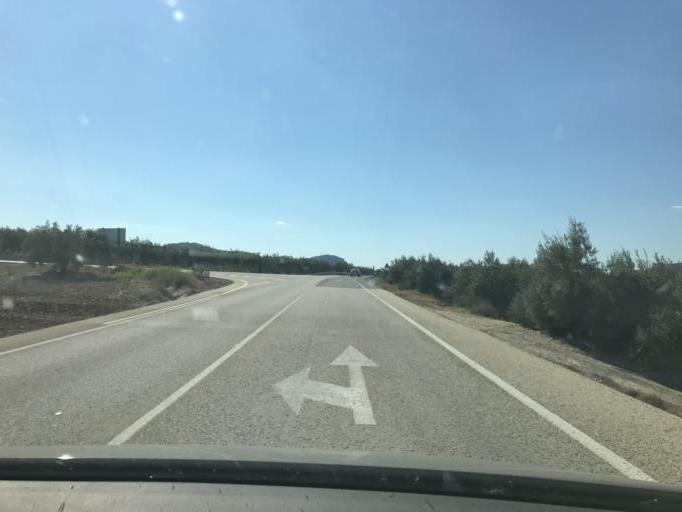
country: ES
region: Andalusia
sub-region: Province of Cordoba
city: Luque
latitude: 37.5636
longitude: -4.2108
